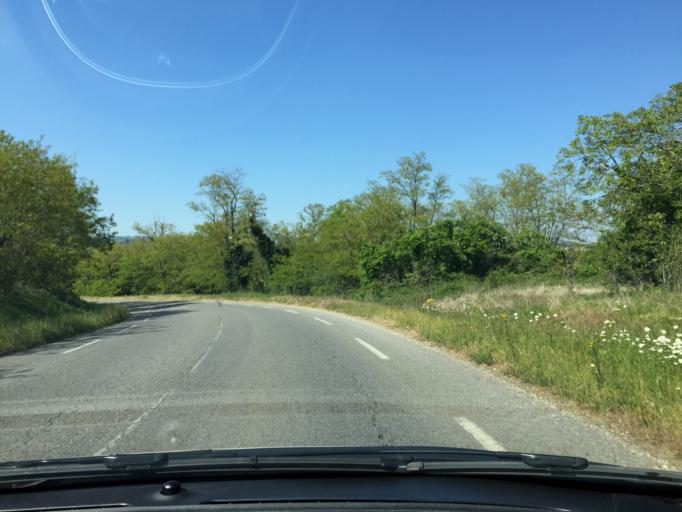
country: FR
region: Rhone-Alpes
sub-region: Departement du Rhone
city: Saint-Andeol-le-Chateau
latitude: 45.5984
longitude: 4.6943
